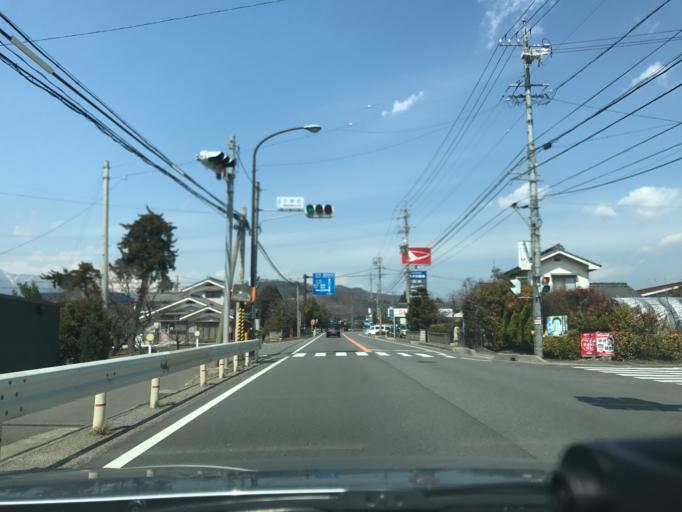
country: JP
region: Nagano
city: Hotaka
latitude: 36.3445
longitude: 137.9226
